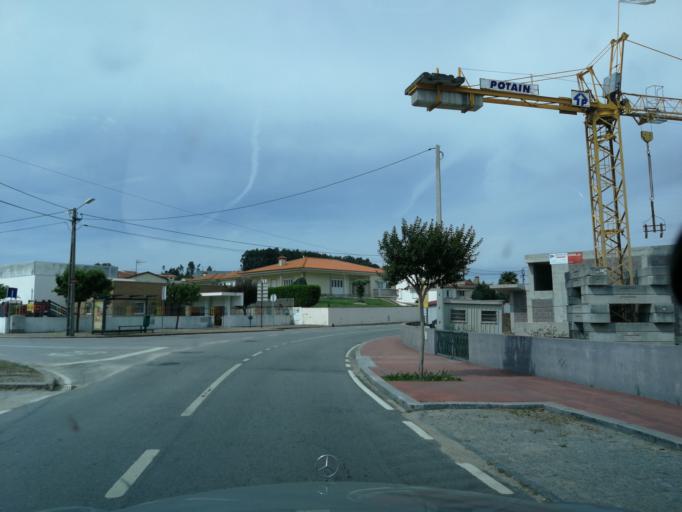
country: PT
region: Braga
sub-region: Vila Nova de Famalicao
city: Calendario
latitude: 41.4134
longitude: -8.5407
